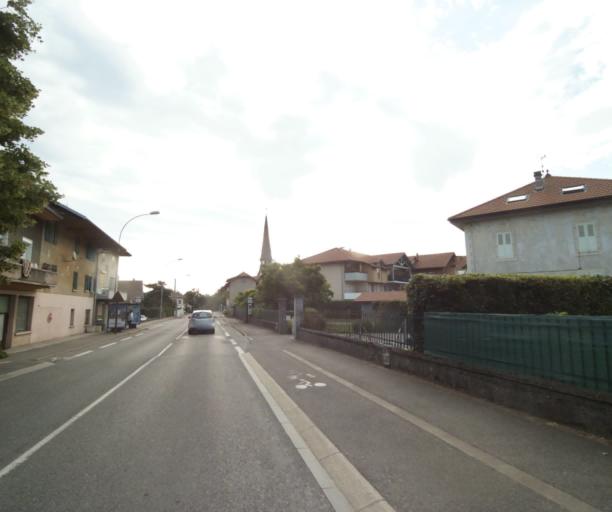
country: FR
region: Rhone-Alpes
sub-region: Departement de la Haute-Savoie
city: Thonon-les-Bains
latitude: 46.3824
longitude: 6.5031
